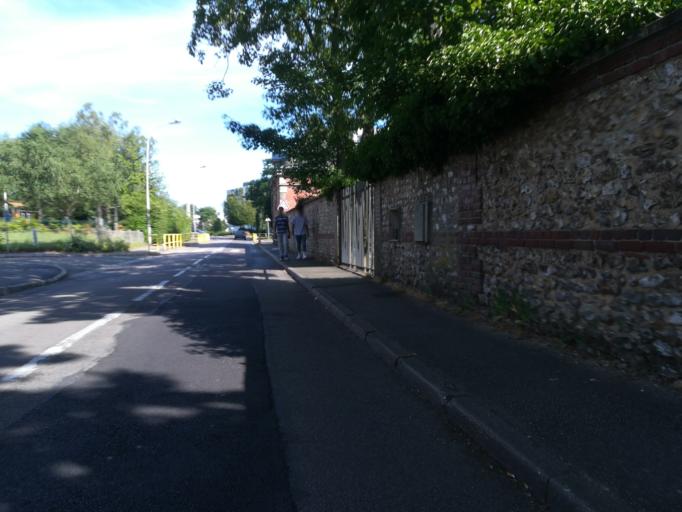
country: FR
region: Haute-Normandie
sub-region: Departement de la Seine-Maritime
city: Deville-les-Rouen
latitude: 49.4639
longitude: 1.0655
